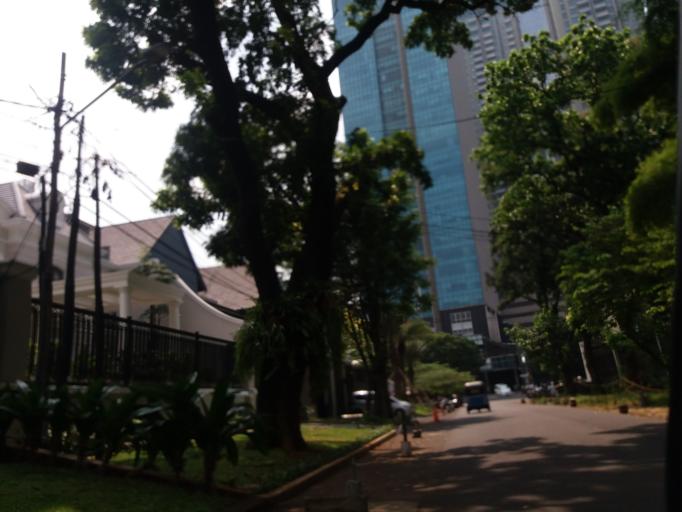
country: ID
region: Jakarta Raya
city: Jakarta
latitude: -6.2309
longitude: 106.8058
